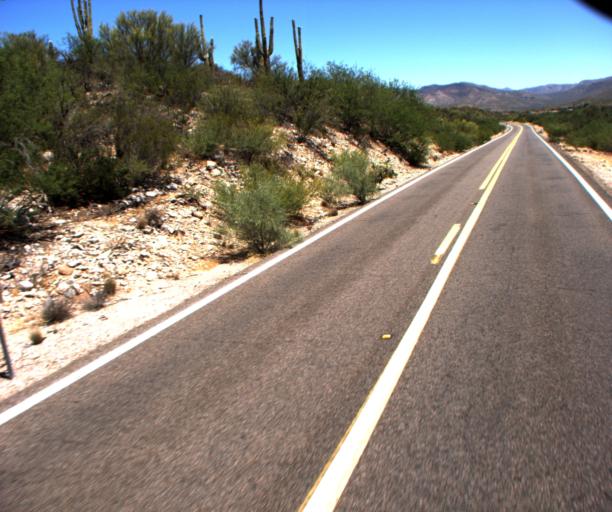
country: US
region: Arizona
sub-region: Pinal County
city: Kearny
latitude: 33.1034
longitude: -110.7483
